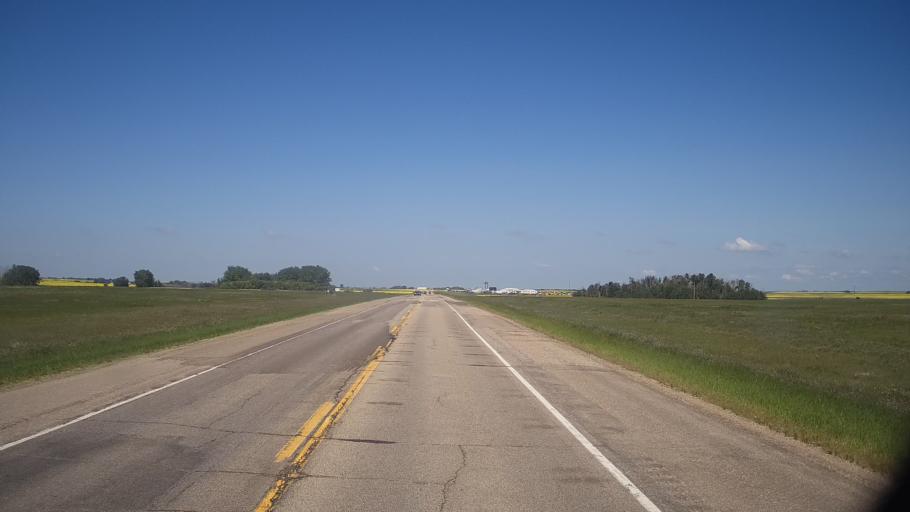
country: CA
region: Saskatchewan
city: Saskatoon
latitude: 51.9963
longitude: -106.1033
